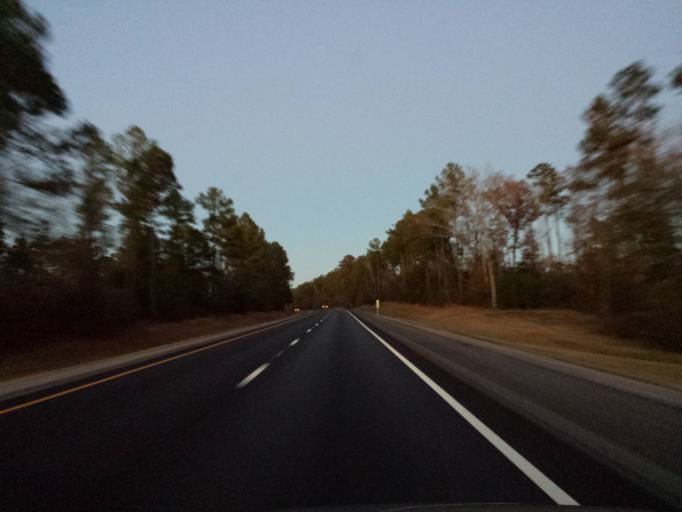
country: US
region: Mississippi
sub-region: Jones County
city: Sharon
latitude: 31.7606
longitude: -89.0630
